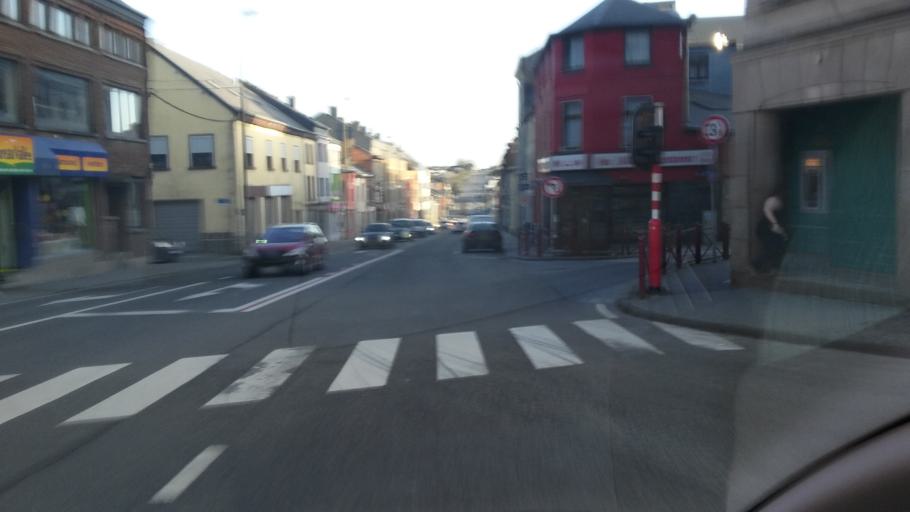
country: BE
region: Wallonia
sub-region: Province du Luxembourg
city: Bastogne
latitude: 50.0005
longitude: 5.7152
